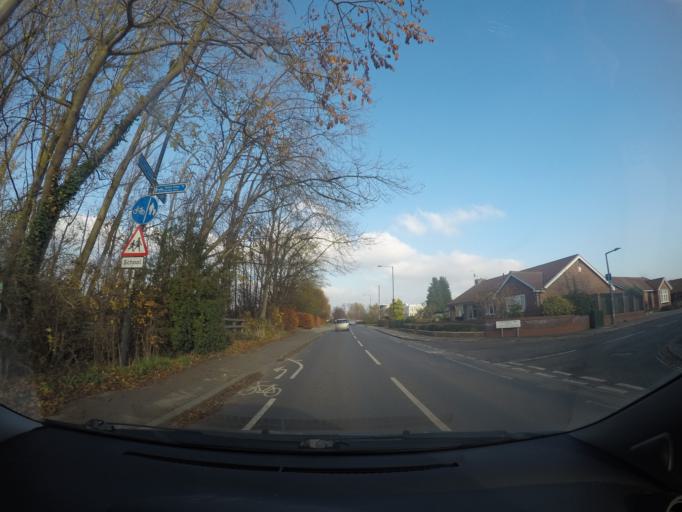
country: GB
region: England
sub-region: City of York
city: Huntington
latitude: 53.9891
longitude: -1.0675
